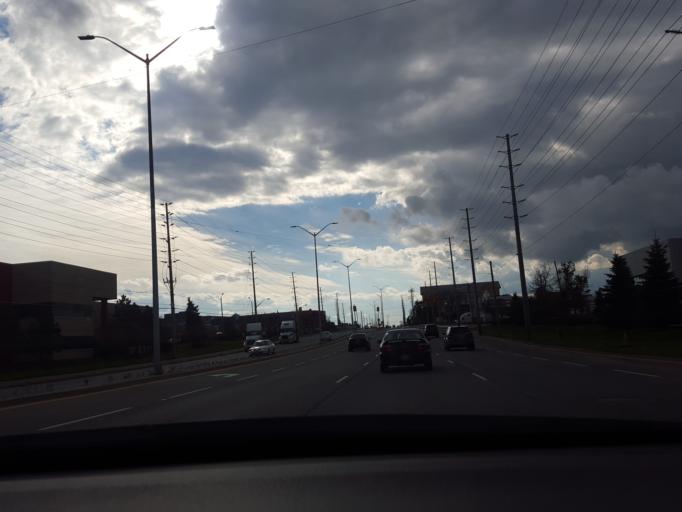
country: CA
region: Ontario
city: Brampton
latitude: 43.6534
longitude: -79.6981
